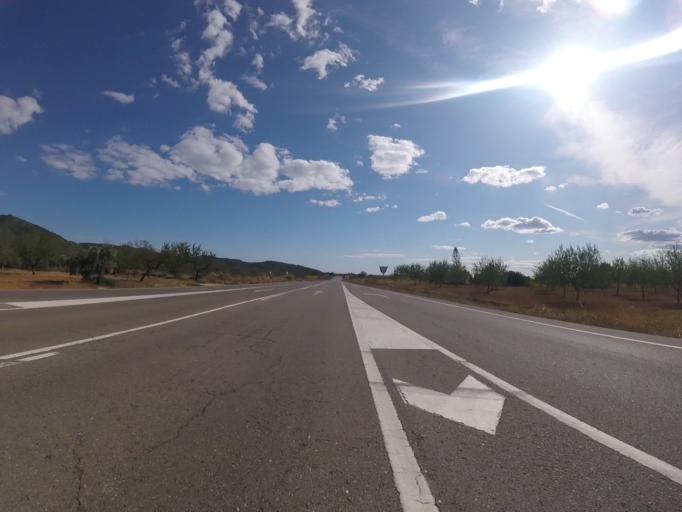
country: ES
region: Valencia
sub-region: Provincia de Castello
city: Alcala de Xivert
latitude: 40.2660
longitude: 0.2418
